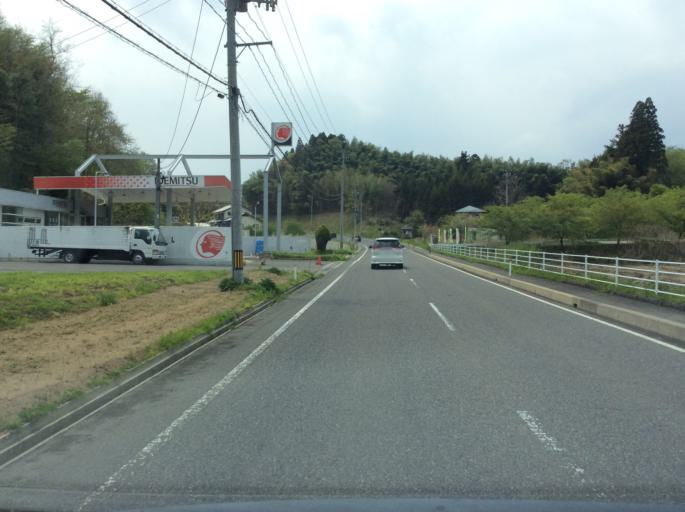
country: JP
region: Fukushima
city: Miharu
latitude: 37.3980
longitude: 140.4950
